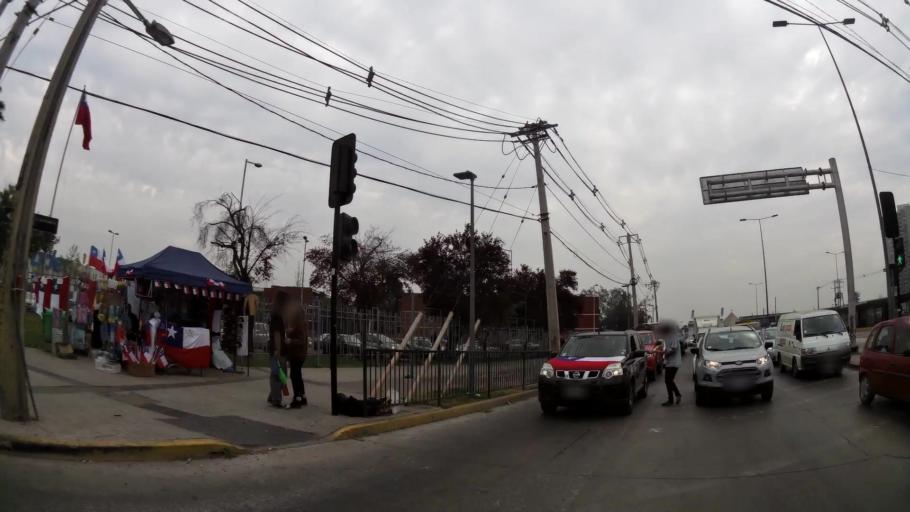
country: CL
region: Santiago Metropolitan
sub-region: Provincia de Santiago
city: Villa Presidente Frei, Nunoa, Santiago, Chile
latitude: -33.5105
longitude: -70.5907
